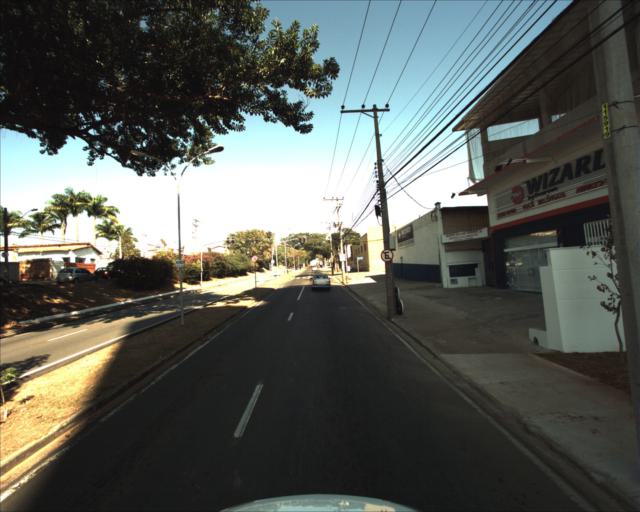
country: BR
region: Sao Paulo
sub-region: Sorocaba
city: Sorocaba
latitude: -23.4937
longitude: -47.4363
